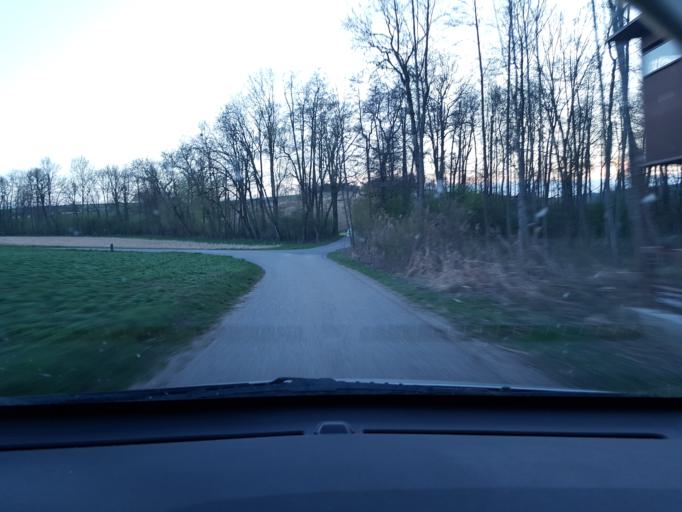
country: AT
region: Upper Austria
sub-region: Politischer Bezirk Linz-Land
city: Ansfelden
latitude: 48.1832
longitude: 14.3303
